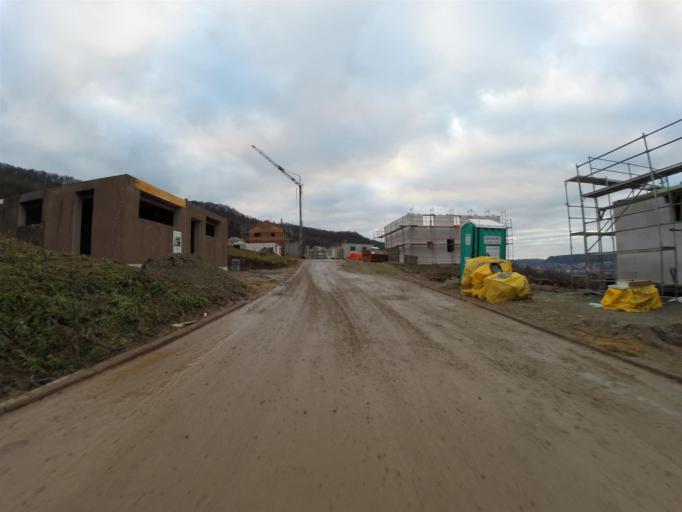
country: DE
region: Thuringia
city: Jena
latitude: 50.9290
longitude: 11.6322
